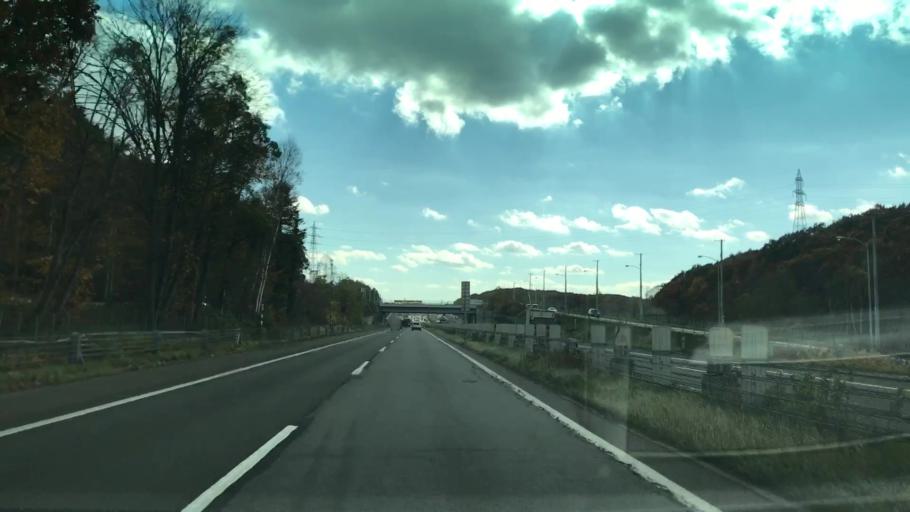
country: JP
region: Hokkaido
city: Kitahiroshima
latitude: 43.0044
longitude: 141.4673
